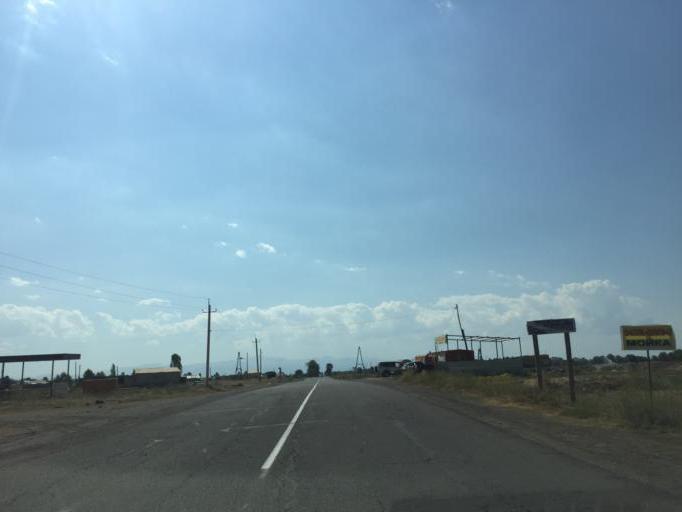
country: AM
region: Geghark'unik'i Marz
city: Tsovinar
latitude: 40.1621
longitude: 45.4796
